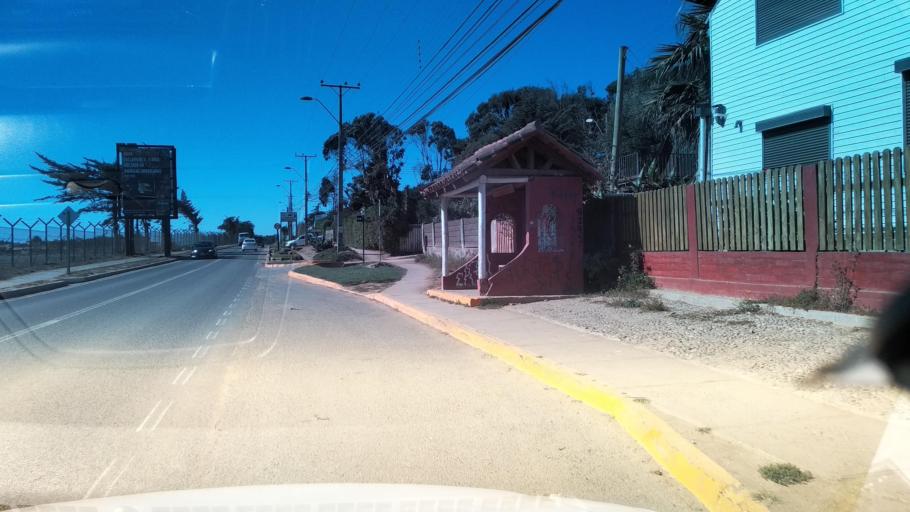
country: CL
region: O'Higgins
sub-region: Provincia de Colchagua
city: Santa Cruz
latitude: -34.3992
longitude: -72.0223
